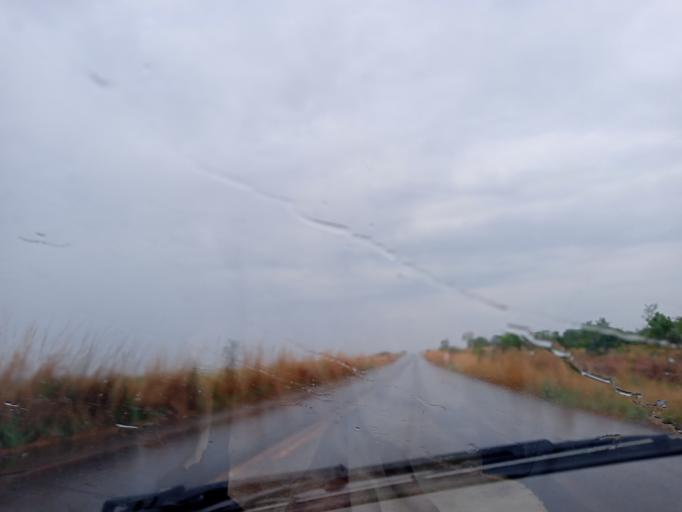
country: BR
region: Minas Gerais
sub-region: Ituiutaba
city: Ituiutaba
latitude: -19.0805
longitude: -49.5063
